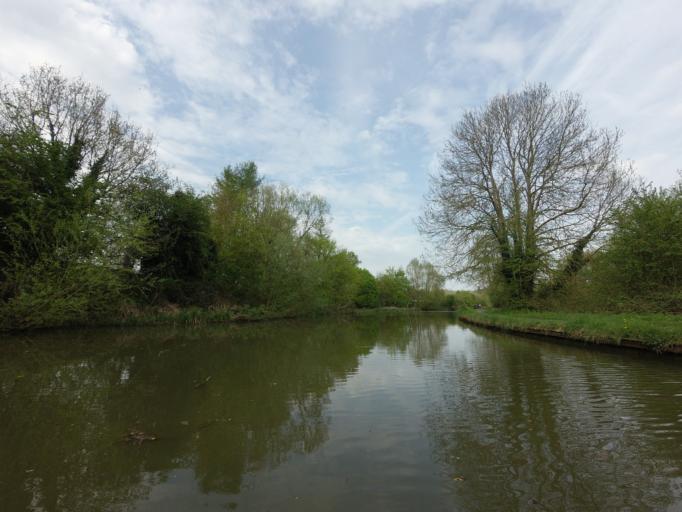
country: GB
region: England
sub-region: Central Bedfordshire
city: Leighton Buzzard
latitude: 51.9309
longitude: -0.6770
